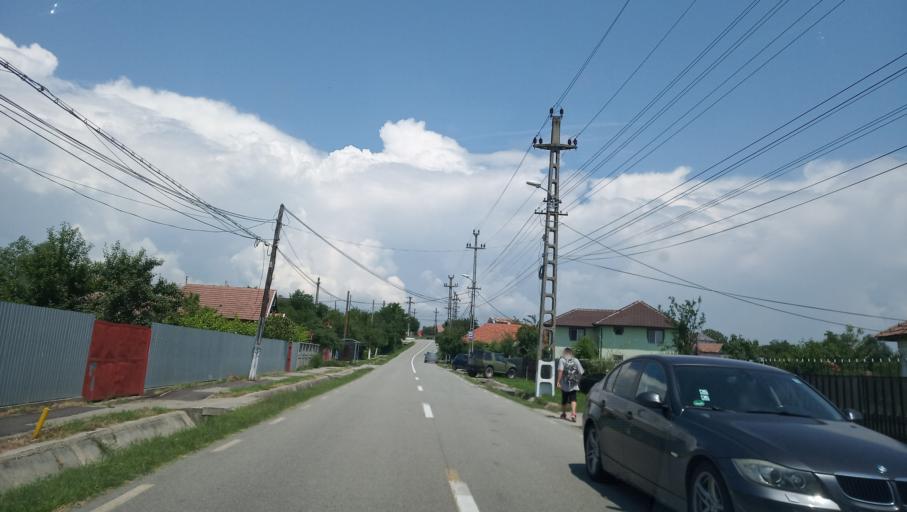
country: RO
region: Gorj
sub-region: Comuna Turcinesti
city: Turcinesti
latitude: 45.0622
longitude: 23.3485
